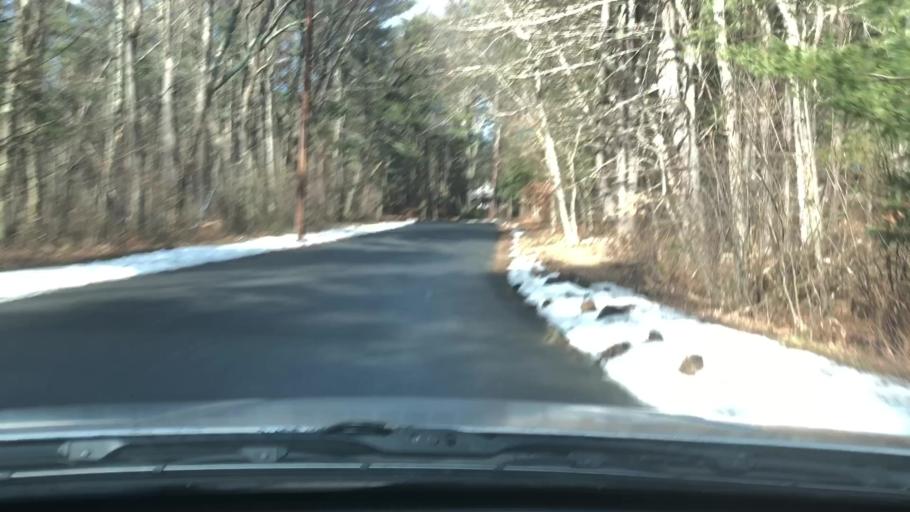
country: US
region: Massachusetts
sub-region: Middlesex County
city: West Concord
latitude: 42.5000
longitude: -71.3930
